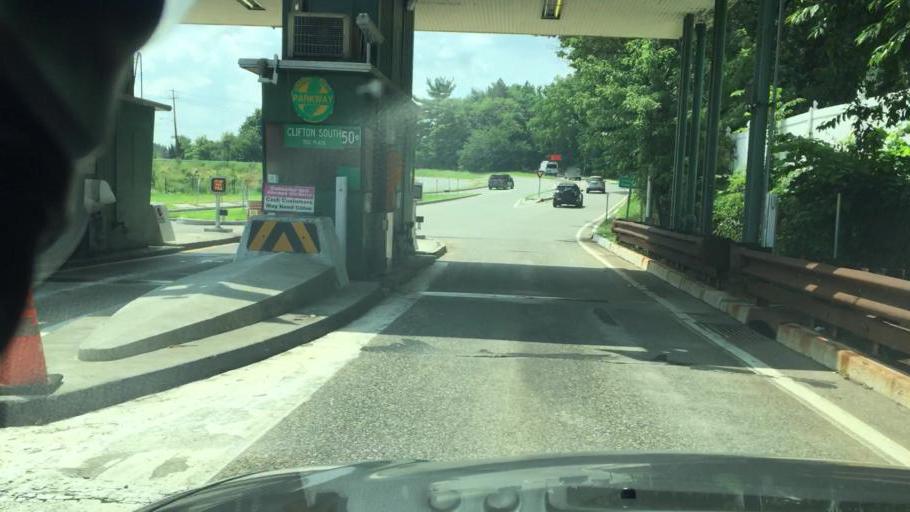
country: US
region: New Jersey
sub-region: Passaic County
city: Clifton
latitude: 40.8771
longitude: -74.1689
